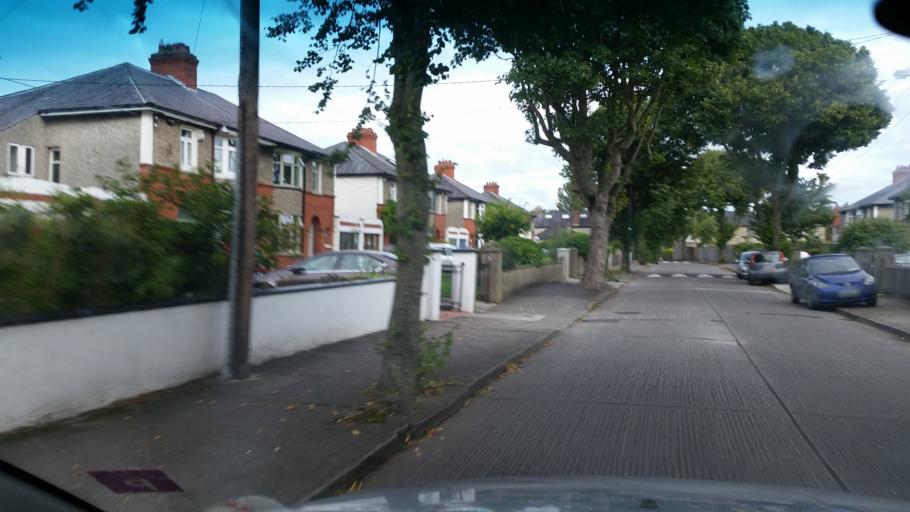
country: IE
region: Leinster
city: Glasnevin
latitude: 53.3831
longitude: -6.2681
